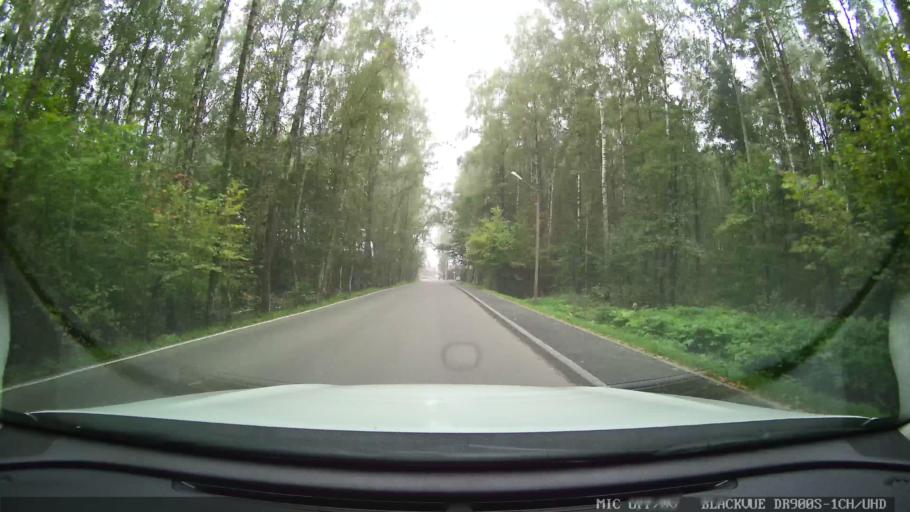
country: RU
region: Moscow
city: Novo-Peredelkino
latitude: 55.6183
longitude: 37.3280
